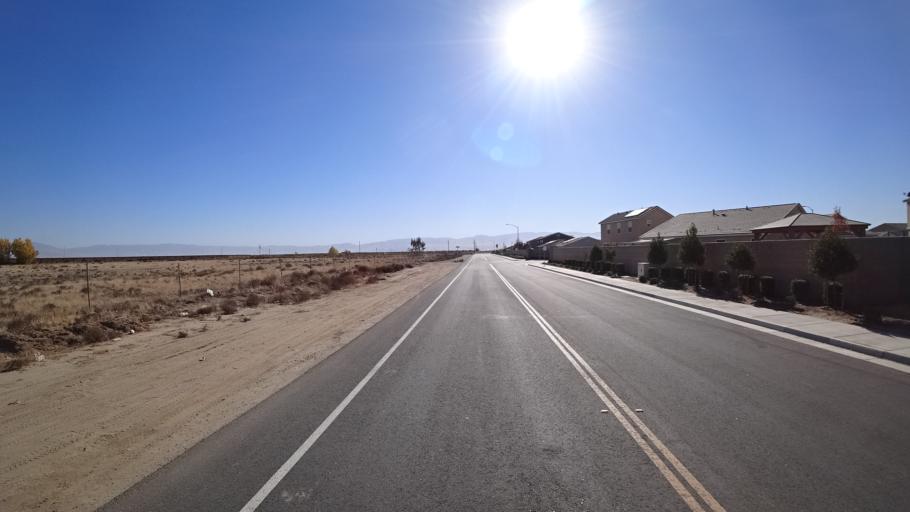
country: US
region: California
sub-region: Kern County
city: Greenfield
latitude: 35.2661
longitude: -119.0656
